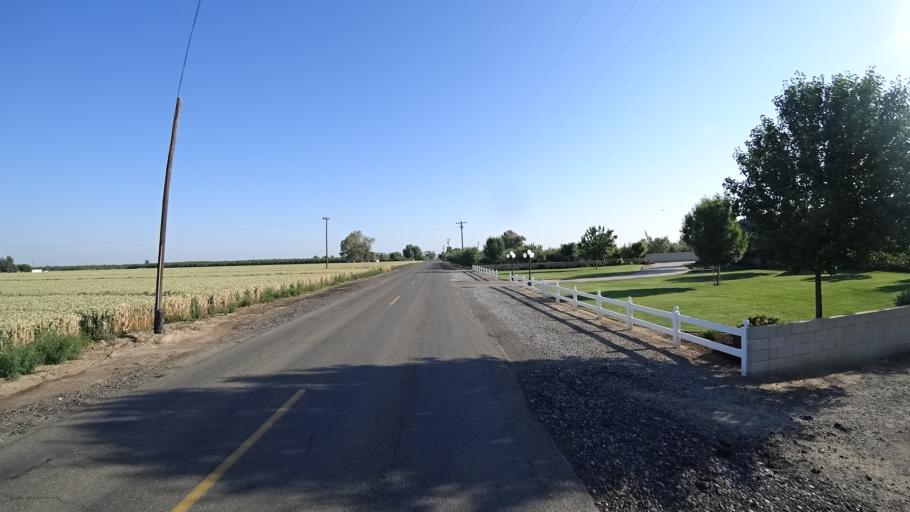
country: US
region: California
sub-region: Kings County
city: Lemoore
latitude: 36.2810
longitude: -119.7447
